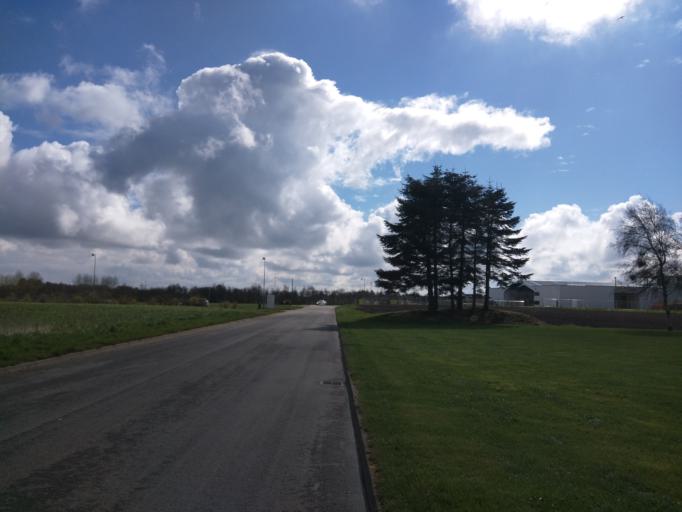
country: DK
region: South Denmark
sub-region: Fredericia Kommune
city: Snoghoj
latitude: 55.5386
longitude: 9.6975
